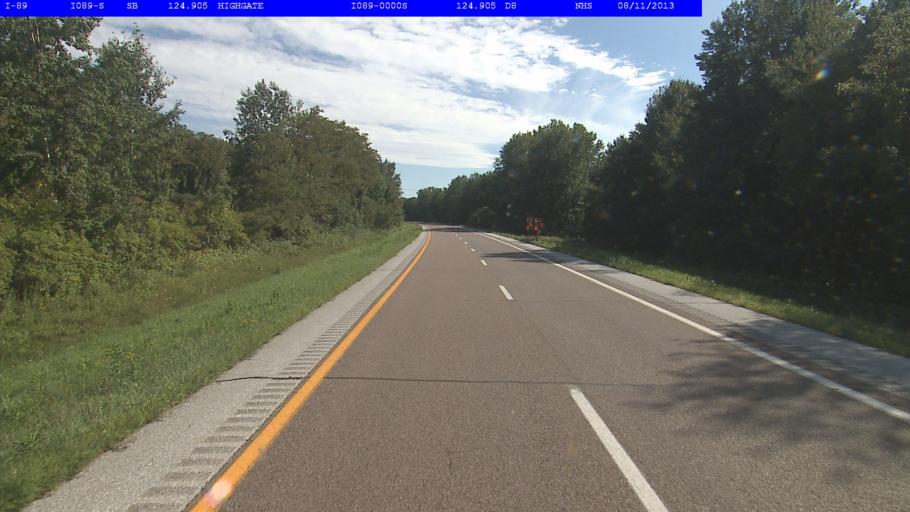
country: US
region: Vermont
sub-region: Franklin County
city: Swanton
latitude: 44.9436
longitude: -73.1149
